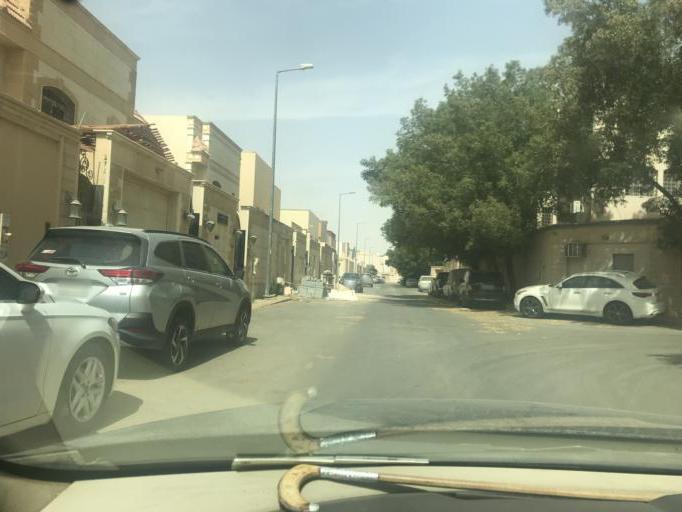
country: SA
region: Ar Riyad
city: Riyadh
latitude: 24.8017
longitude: 46.6634
